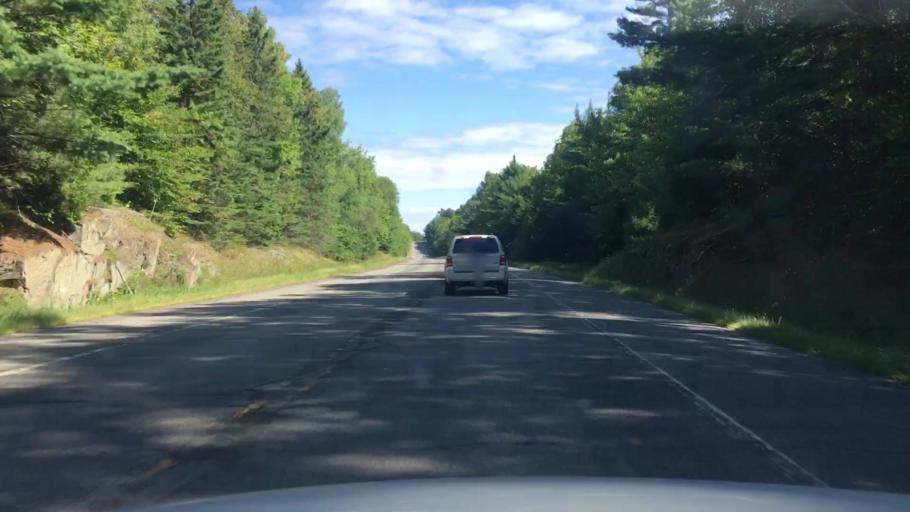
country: US
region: Maine
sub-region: Penobscot County
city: Dexter
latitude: 45.0530
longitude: -69.2592
